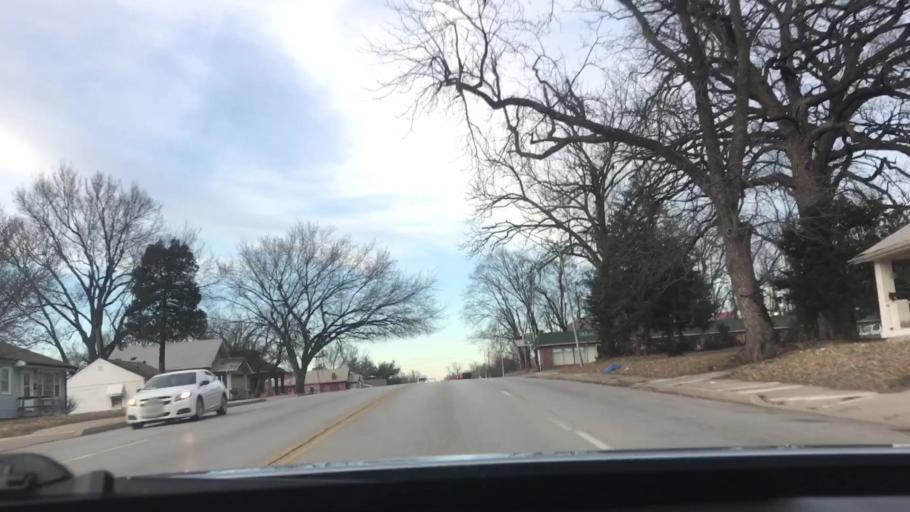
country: US
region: Missouri
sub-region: Jackson County
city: Sugar Creek
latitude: 39.0774
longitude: -94.4462
